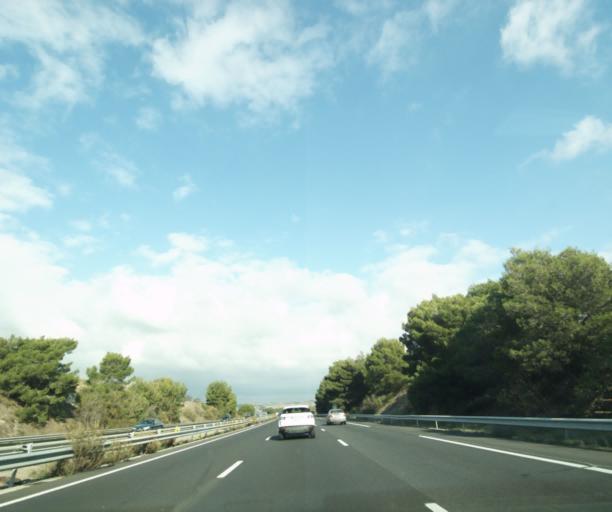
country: FR
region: Languedoc-Roussillon
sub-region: Departement de l'Aude
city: Fleury
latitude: 43.2384
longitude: 3.1432
